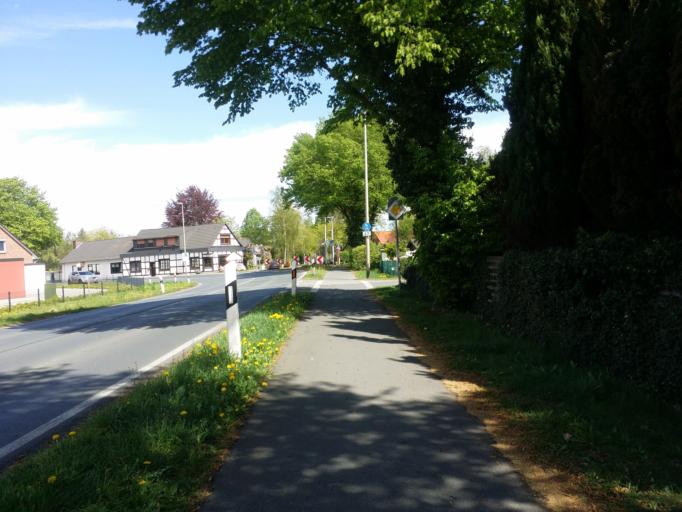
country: DE
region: Lower Saxony
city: Delmenhorst
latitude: 53.0850
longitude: 8.6502
